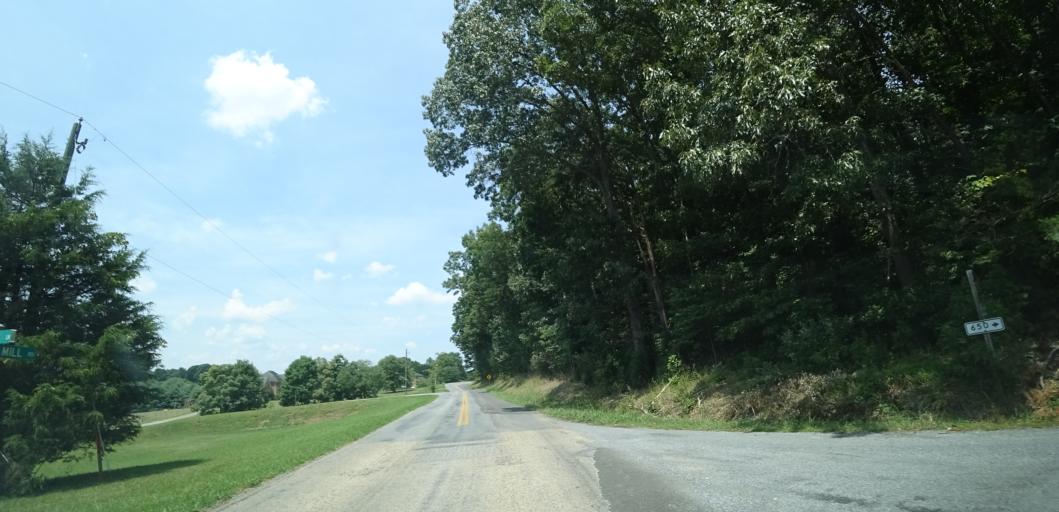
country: US
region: Virginia
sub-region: Botetourt County
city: Fincastle
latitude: 37.4744
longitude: -79.8458
